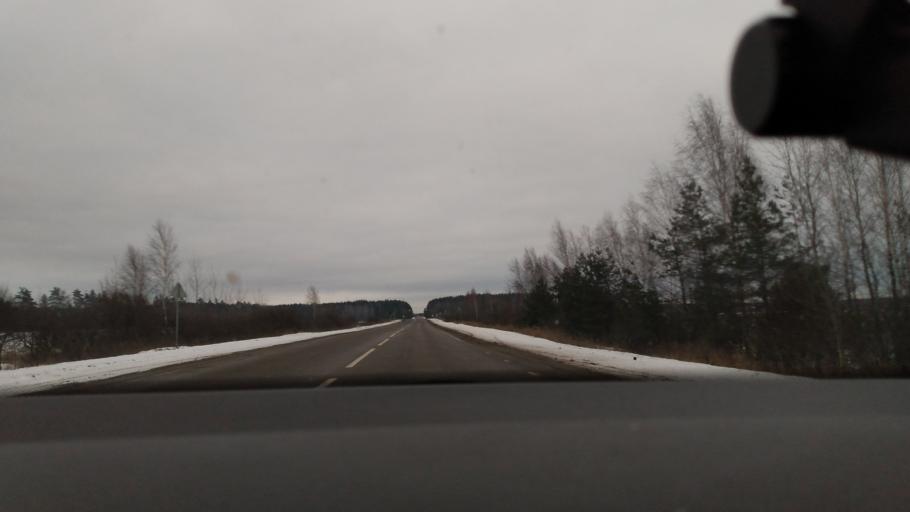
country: RU
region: Moskovskaya
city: Yegor'yevsk
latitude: 55.4379
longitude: 39.0222
